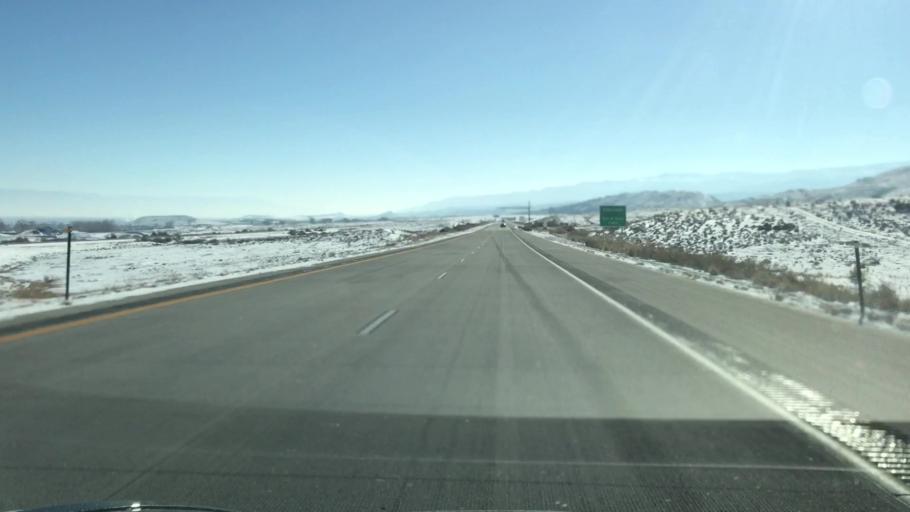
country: US
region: Colorado
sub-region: Mesa County
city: Loma
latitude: 39.1876
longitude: -108.8370
